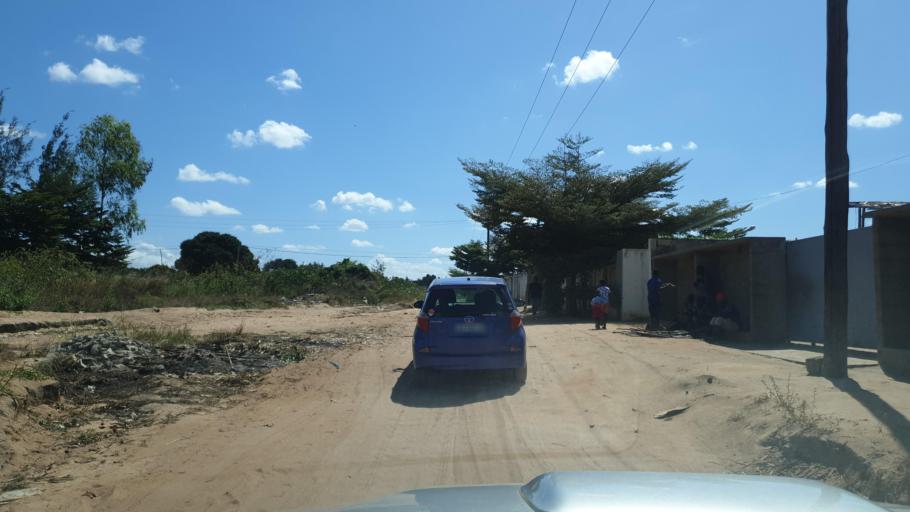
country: MZ
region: Nampula
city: Nampula
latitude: -15.1050
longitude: 39.2062
